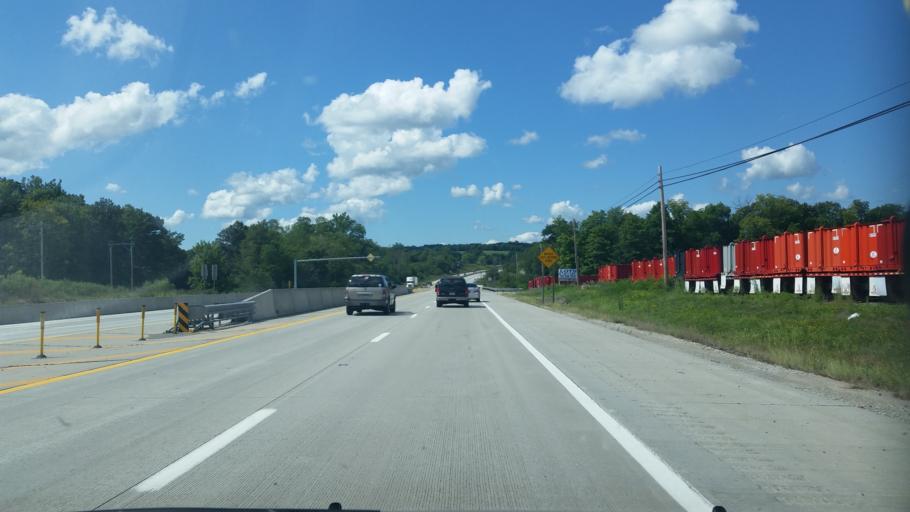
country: US
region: Pennsylvania
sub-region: Indiana County
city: Blairsville
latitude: 40.4325
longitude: -79.2863
